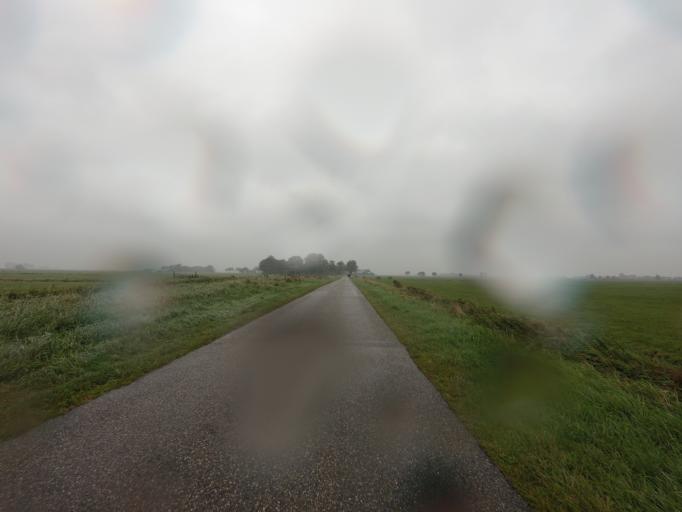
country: NL
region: Friesland
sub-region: Gemeente Boarnsterhim
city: Aldeboarn
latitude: 53.0668
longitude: 5.9221
